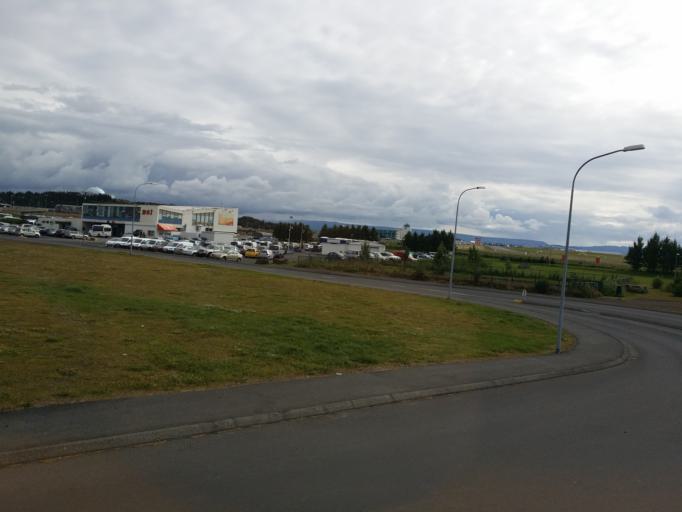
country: IS
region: Capital Region
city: Kopavogur
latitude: 64.1387
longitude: -21.9366
